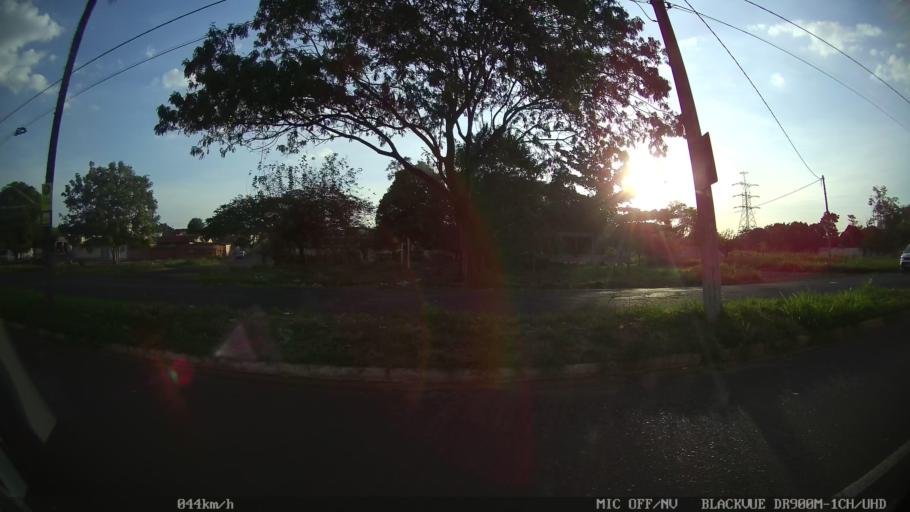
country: BR
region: Sao Paulo
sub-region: Ribeirao Preto
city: Ribeirao Preto
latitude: -21.1211
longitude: -47.8030
